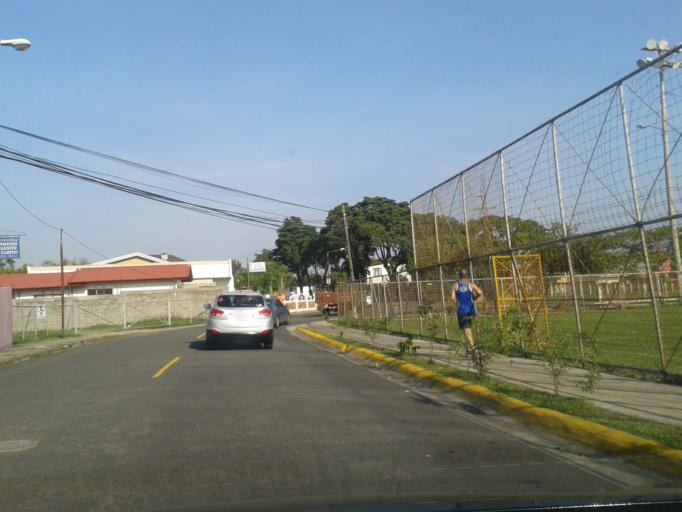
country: CR
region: Heredia
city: Llorente
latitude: 10.0137
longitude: -84.1498
